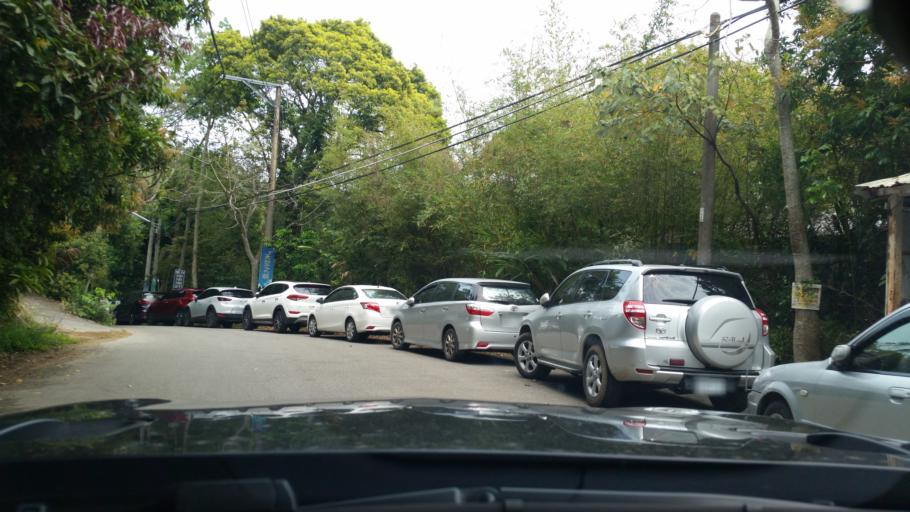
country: TW
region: Taiwan
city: Fengyuan
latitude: 24.3478
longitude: 120.7797
